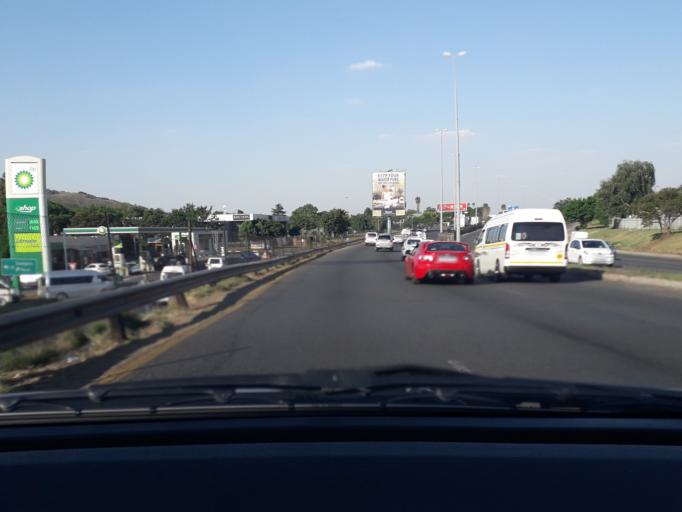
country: ZA
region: Gauteng
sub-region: City of Johannesburg Metropolitan Municipality
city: Johannesburg
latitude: -26.1785
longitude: 28.1146
